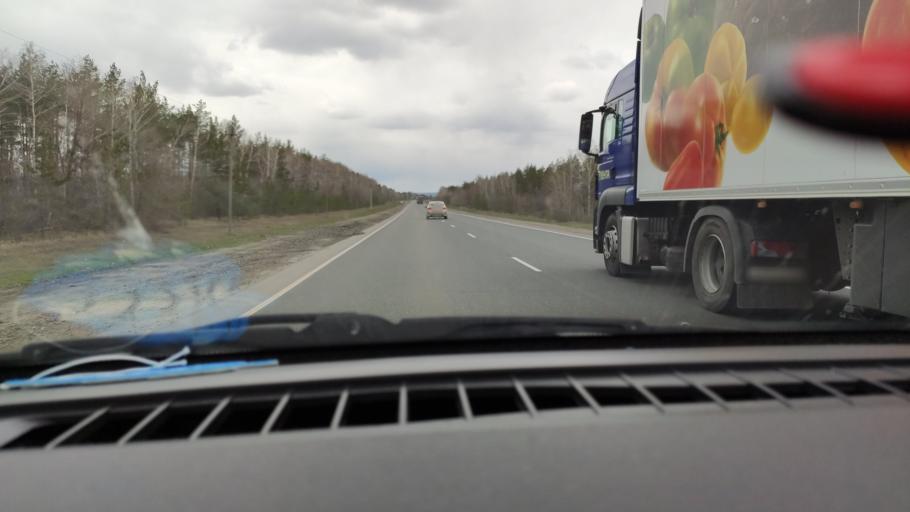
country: RU
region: Saratov
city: Sennoy
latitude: 52.1531
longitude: 47.0057
